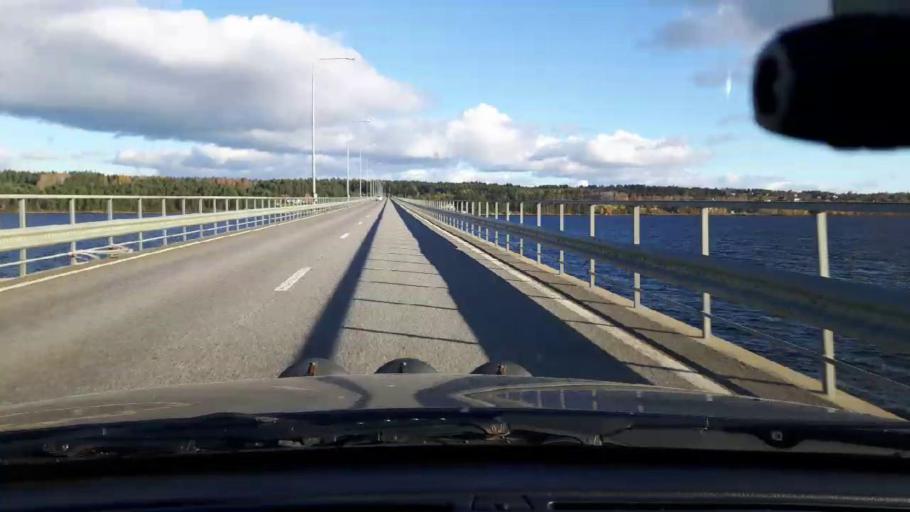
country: SE
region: Jaemtland
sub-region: Bergs Kommun
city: Hoverberg
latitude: 62.9781
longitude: 14.4636
